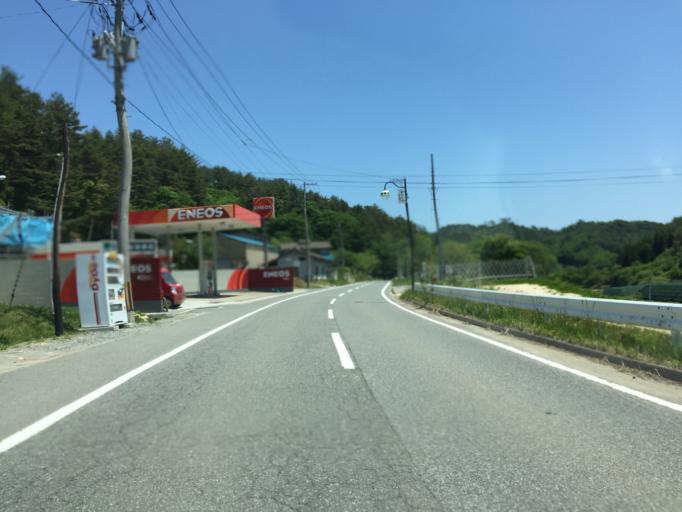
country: JP
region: Fukushima
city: Funehikimachi-funehiki
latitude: 37.5032
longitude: 140.7678
